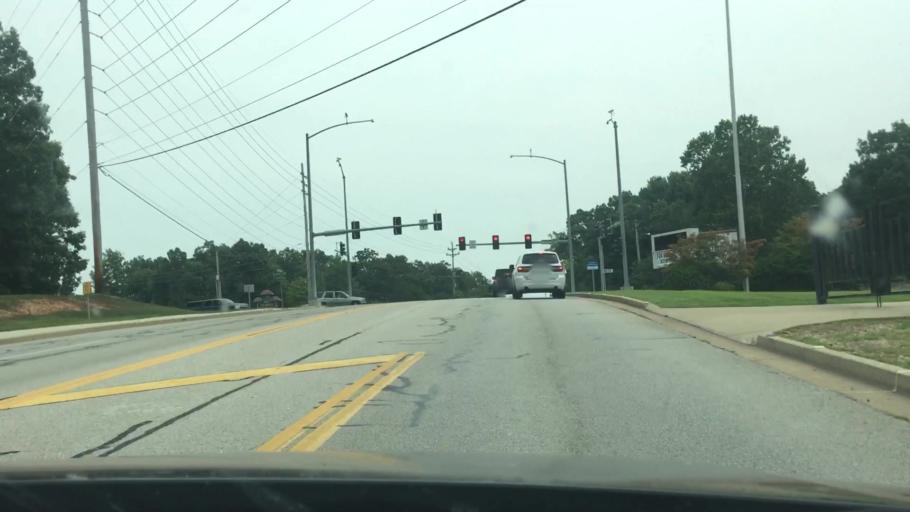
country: US
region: Missouri
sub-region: Miller County
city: Lake Ozark
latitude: 38.1920
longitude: -92.6667
